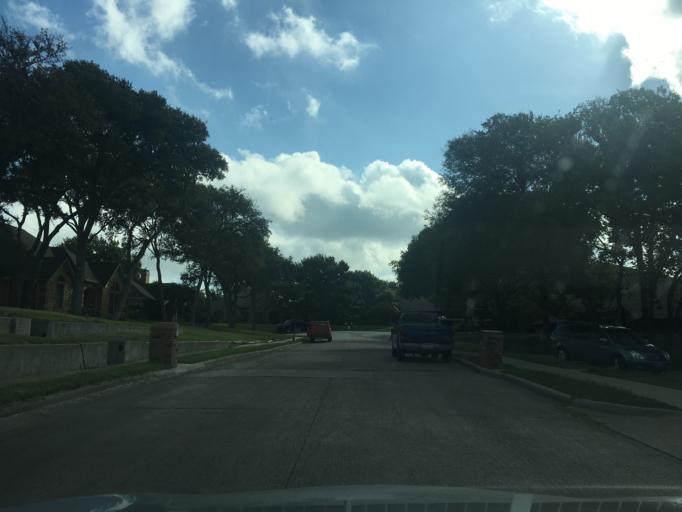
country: US
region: Texas
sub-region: Dallas County
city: Sachse
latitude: 32.9675
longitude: -96.5925
